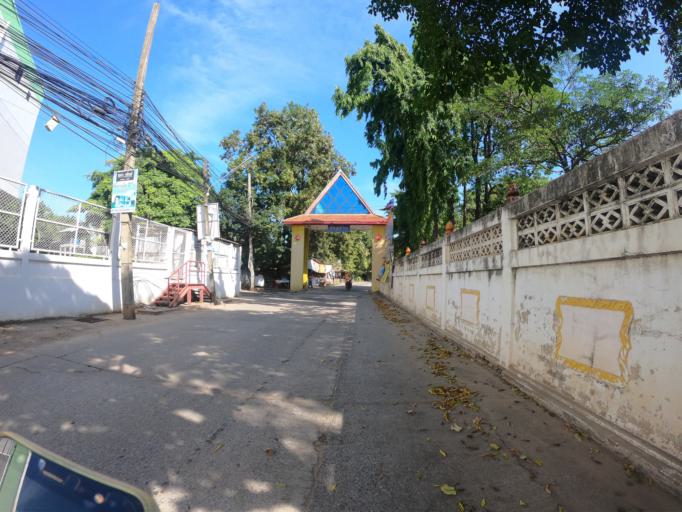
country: TH
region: Nakhon Ratchasima
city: Nakhon Ratchasima
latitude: 14.9822
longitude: 102.0929
